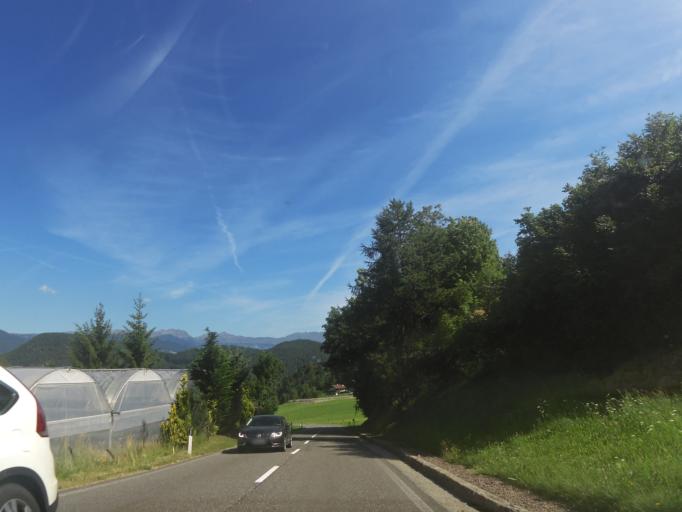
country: IT
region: Trentino-Alto Adige
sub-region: Bolzano
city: Castelrotto
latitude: 46.5585
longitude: 11.5552
